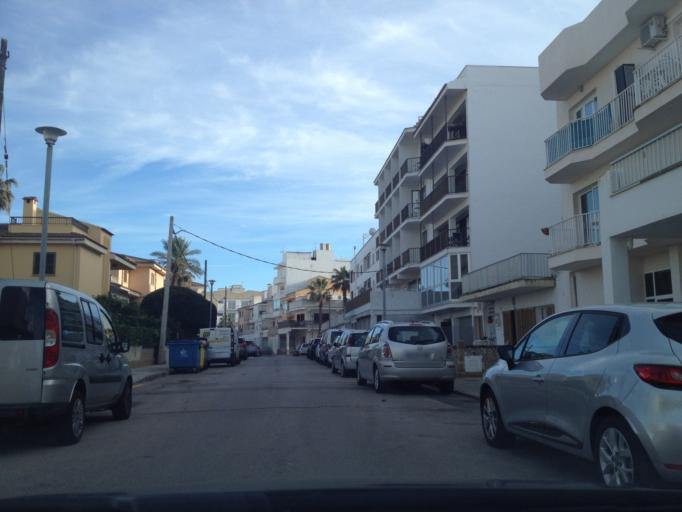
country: ES
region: Balearic Islands
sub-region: Illes Balears
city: Port d'Alcudia
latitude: 39.7686
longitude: 3.1500
